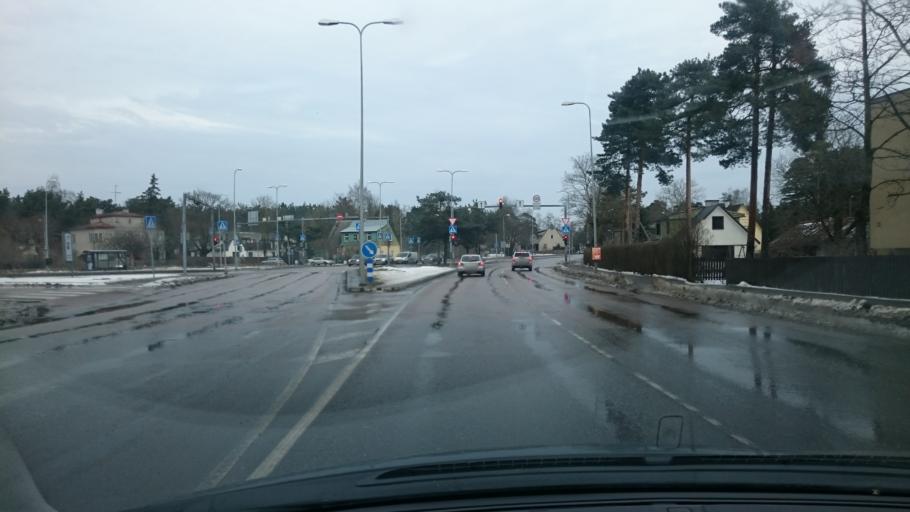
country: EE
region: Harju
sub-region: Tallinna linn
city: Tallinn
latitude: 59.3874
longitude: 24.7184
